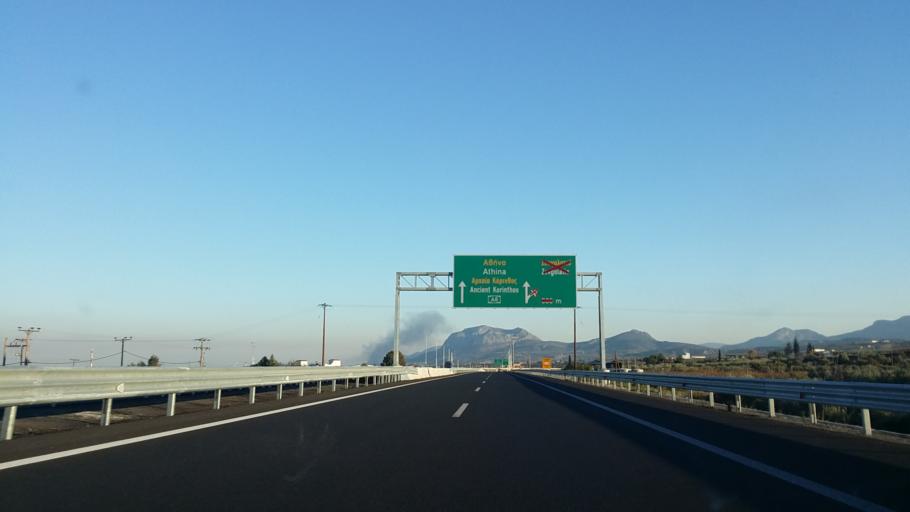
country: GR
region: Peloponnese
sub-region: Nomos Korinthias
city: Vokhaiko
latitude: 37.9331
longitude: 22.7801
